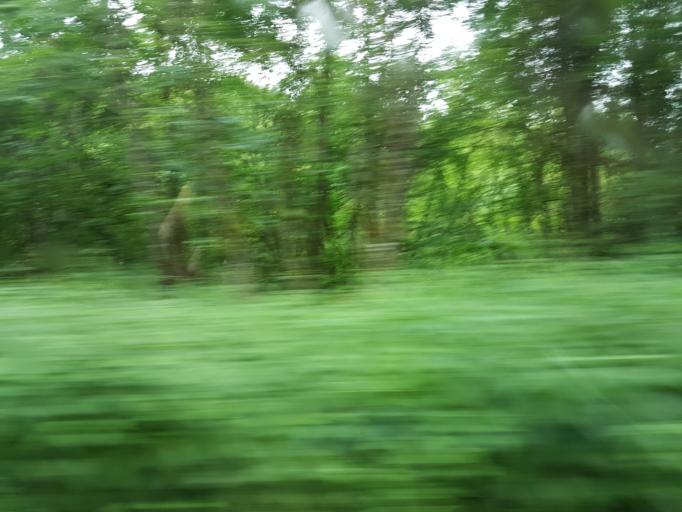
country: FR
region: Bourgogne
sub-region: Departement de la Nievre
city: Corbigny
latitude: 47.1807
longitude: 3.7653
